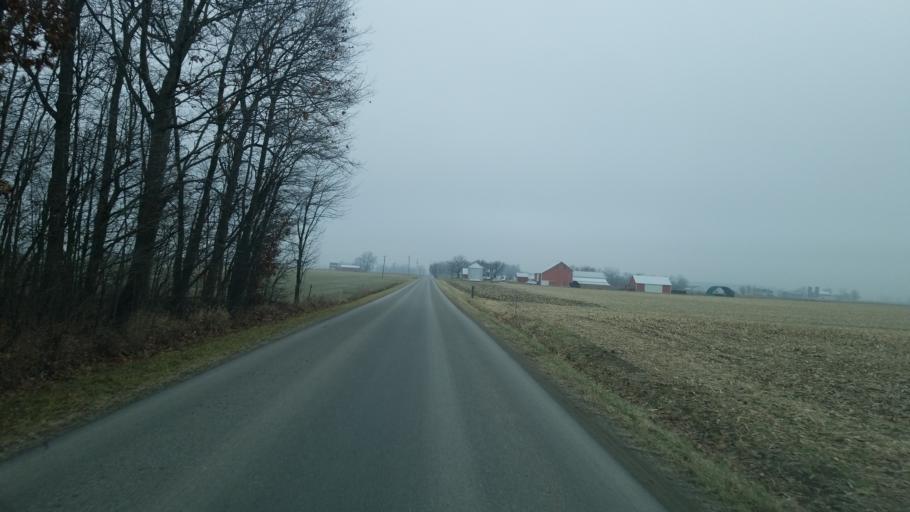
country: US
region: Indiana
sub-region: Adams County
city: Berne
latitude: 40.6628
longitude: -84.9943
